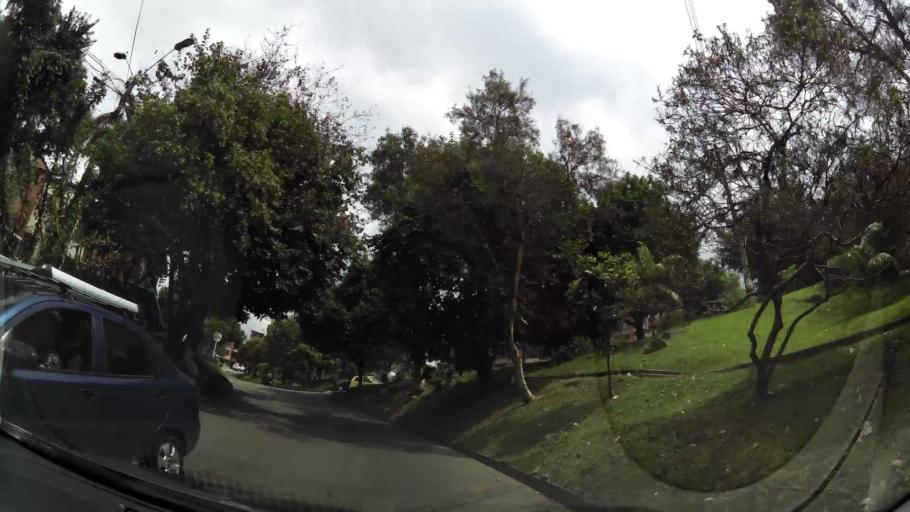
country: CO
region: Antioquia
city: Medellin
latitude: 6.2296
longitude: -75.5448
